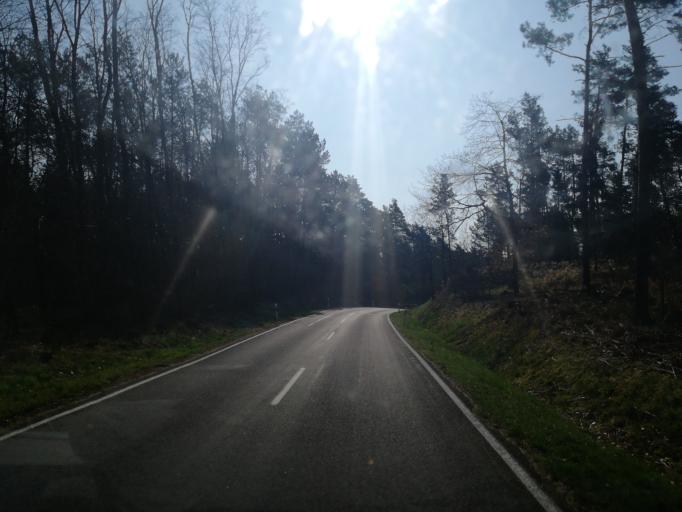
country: DE
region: Brandenburg
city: Sonnewalde
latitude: 51.7632
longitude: 13.6600
